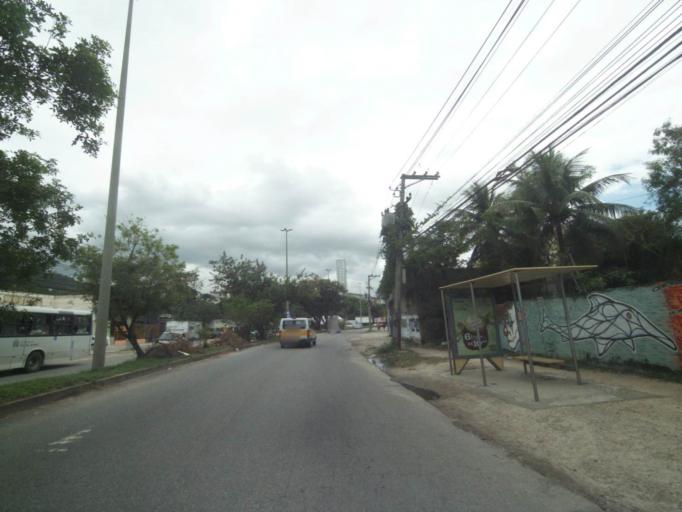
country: BR
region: Rio de Janeiro
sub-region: Nilopolis
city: Nilopolis
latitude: -22.9667
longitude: -43.4121
